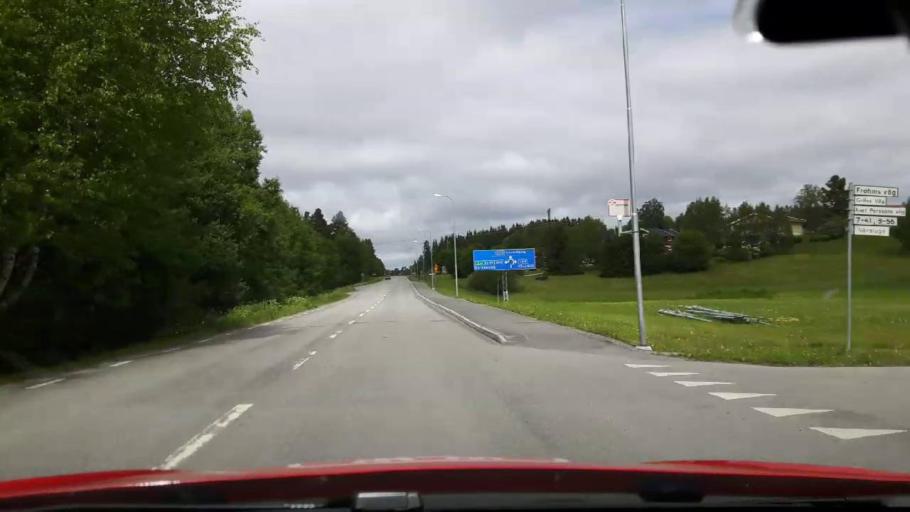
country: SE
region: Jaemtland
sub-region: Krokoms Kommun
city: Krokom
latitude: 63.3339
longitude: 14.4452
